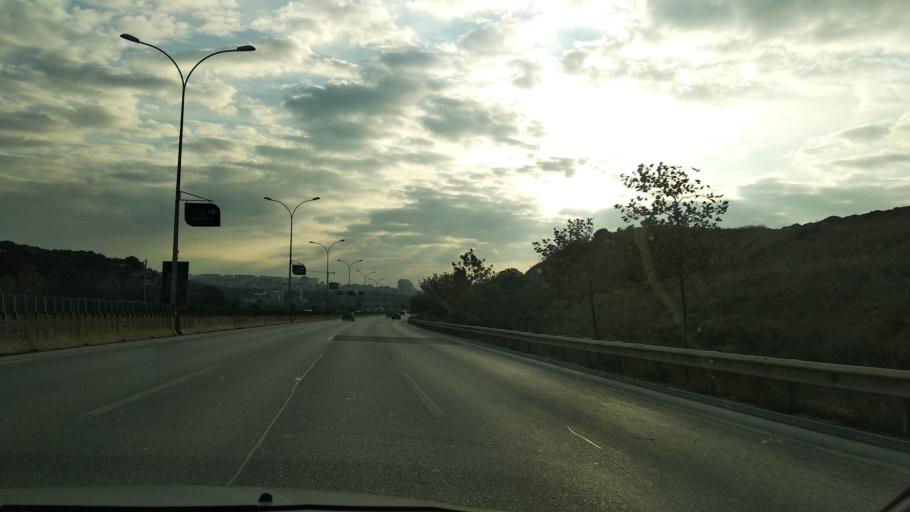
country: TR
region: Istanbul
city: Icmeler
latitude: 40.8850
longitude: 29.3218
